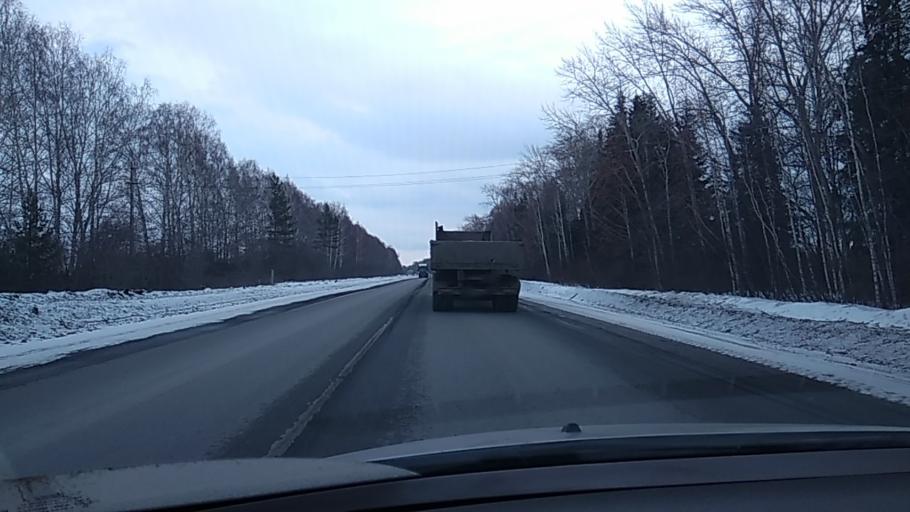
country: RU
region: Sverdlovsk
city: Sovkhoznyy
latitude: 56.5936
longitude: 61.3038
